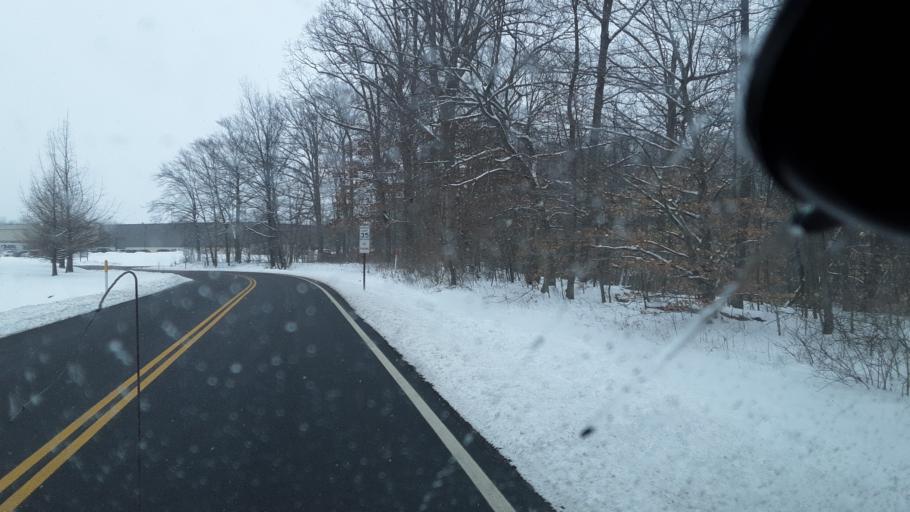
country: US
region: Ohio
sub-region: Licking County
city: Hebron
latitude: 39.9714
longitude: -82.4738
